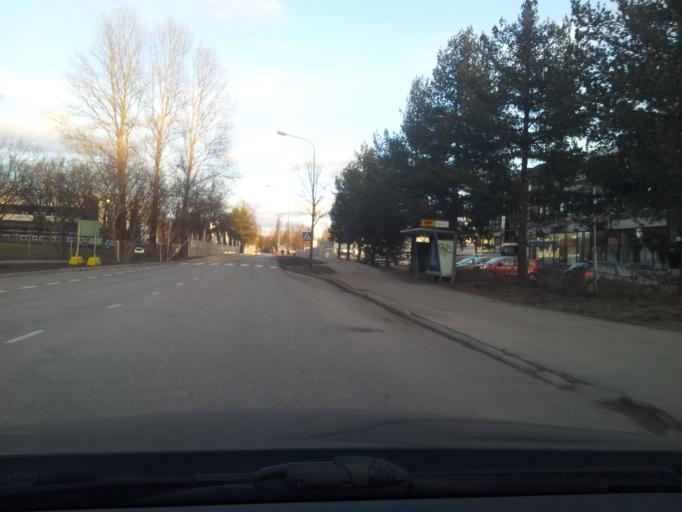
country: FI
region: Uusimaa
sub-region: Helsinki
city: Koukkuniemi
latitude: 60.1727
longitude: 24.7616
